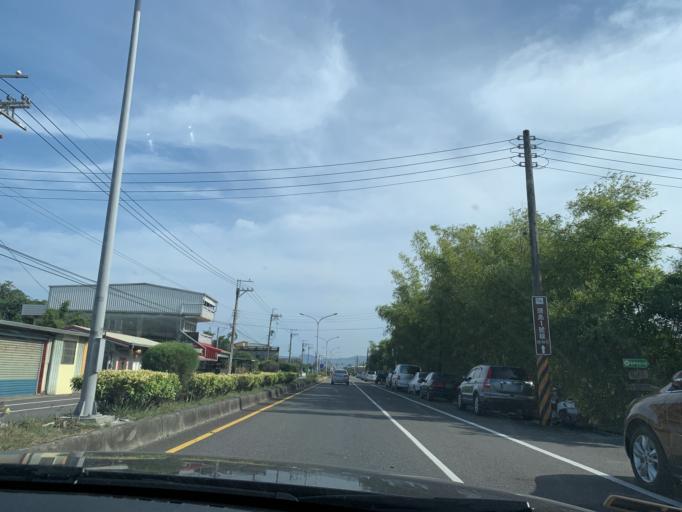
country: TW
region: Taiwan
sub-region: Yilan
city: Yilan
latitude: 24.7462
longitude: 121.8163
